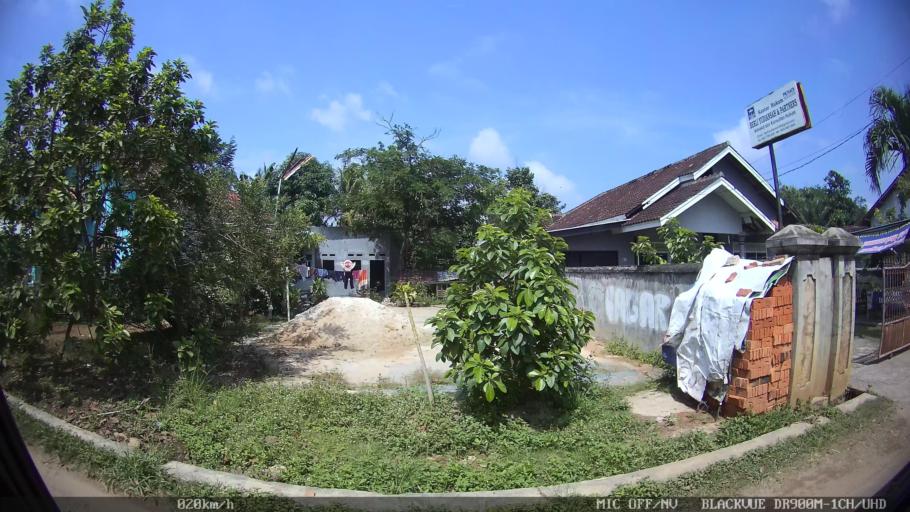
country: ID
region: Lampung
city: Kedaton
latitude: -5.3477
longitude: 105.2889
